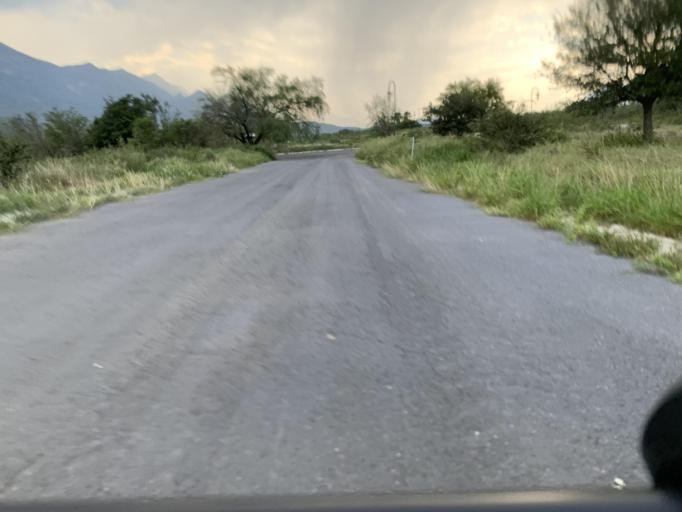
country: MX
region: Nuevo Leon
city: Santiago
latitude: 25.5054
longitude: -100.1804
